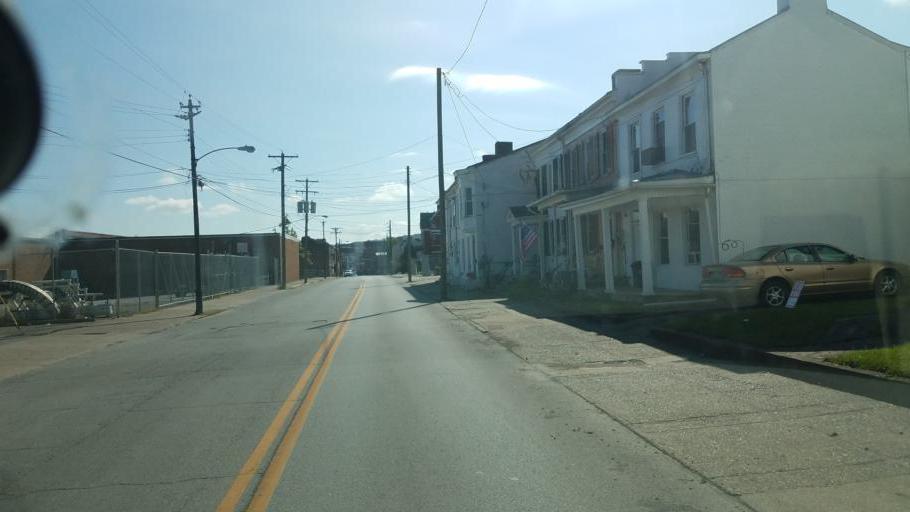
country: US
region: Ohio
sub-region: Brown County
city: Aberdeen
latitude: 38.6509
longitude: -83.7707
